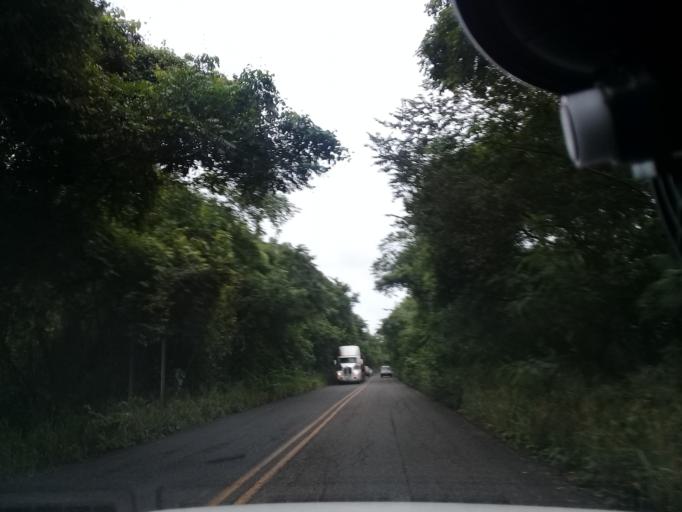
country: MX
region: Veracruz
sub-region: Chalma
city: San Pedro Coyutla
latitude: 21.2194
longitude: -98.3832
